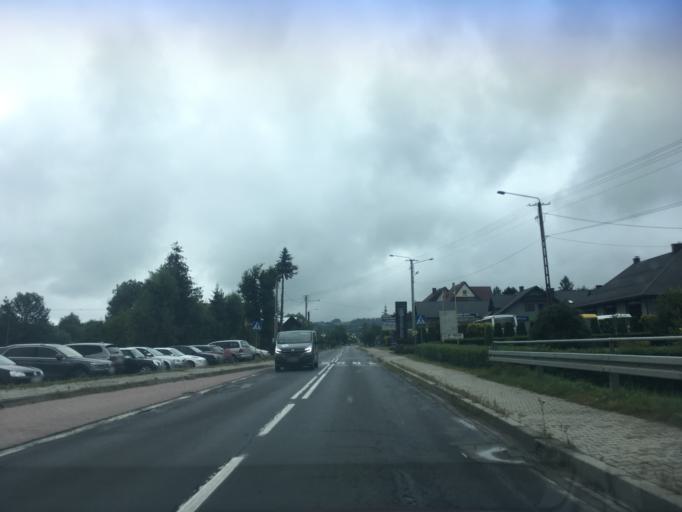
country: PL
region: Lesser Poland Voivodeship
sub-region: Powiat nowotarski
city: Raba Wyzna
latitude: 49.5709
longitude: 19.8914
